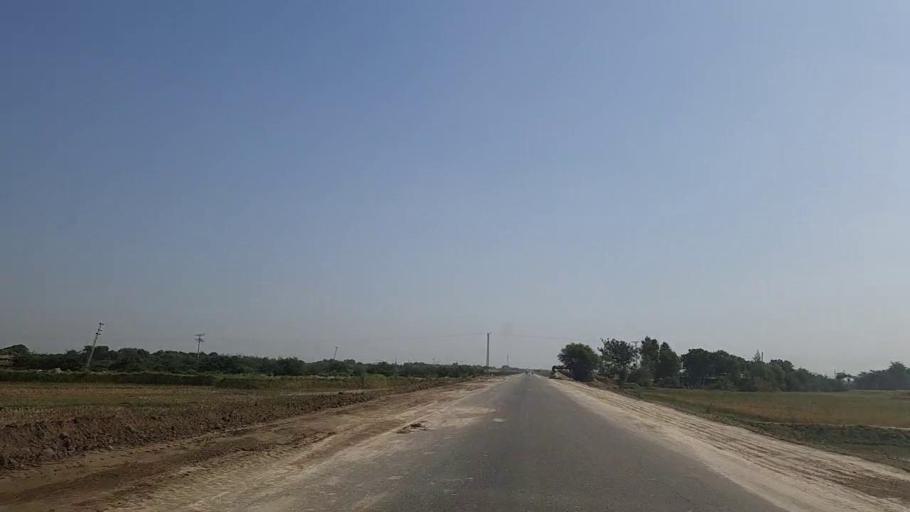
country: PK
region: Sindh
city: Mirpur Batoro
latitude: 24.7508
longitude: 68.2351
